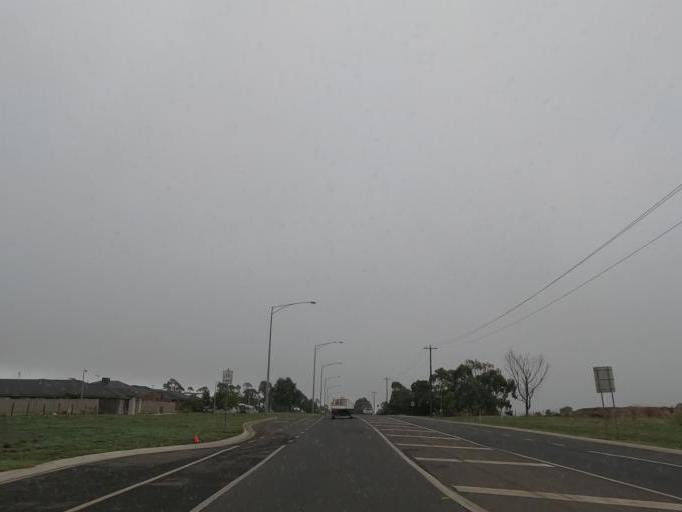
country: AU
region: Victoria
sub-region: Ballarat North
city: Newington
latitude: -37.5620
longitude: 143.8119
